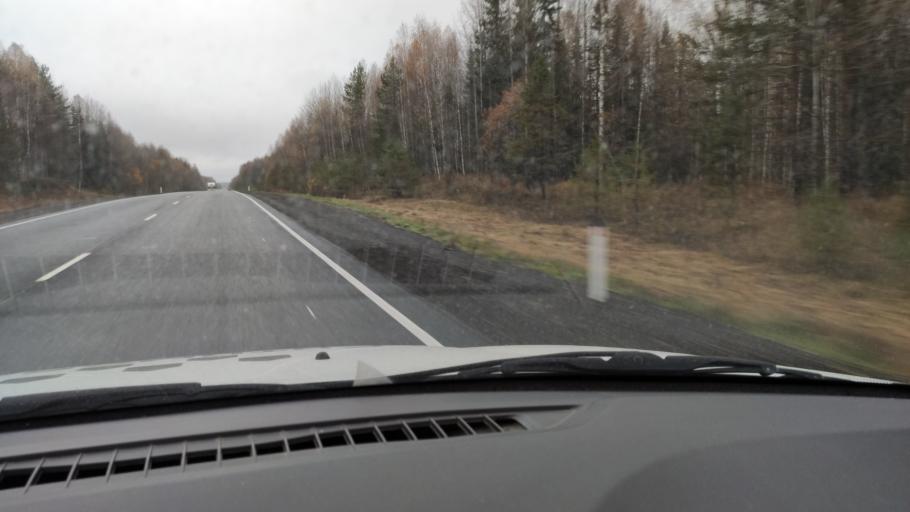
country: RU
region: Kirov
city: Chernaya Kholunitsa
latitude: 58.8820
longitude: 51.4286
